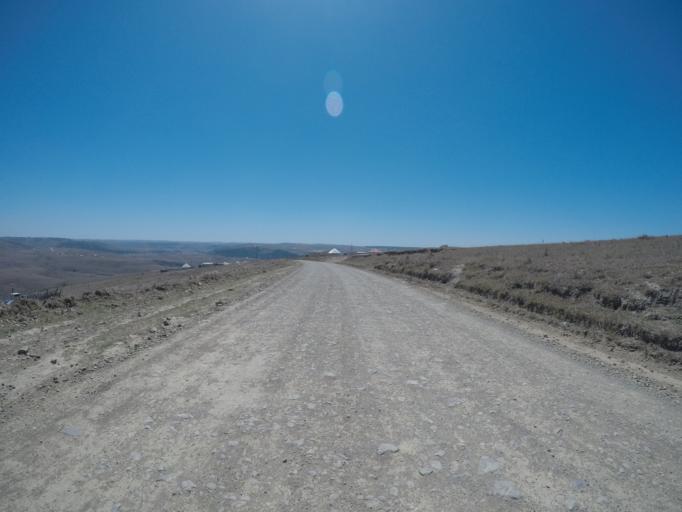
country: ZA
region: Eastern Cape
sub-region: OR Tambo District Municipality
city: Mthatha
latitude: -31.8902
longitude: 28.8775
